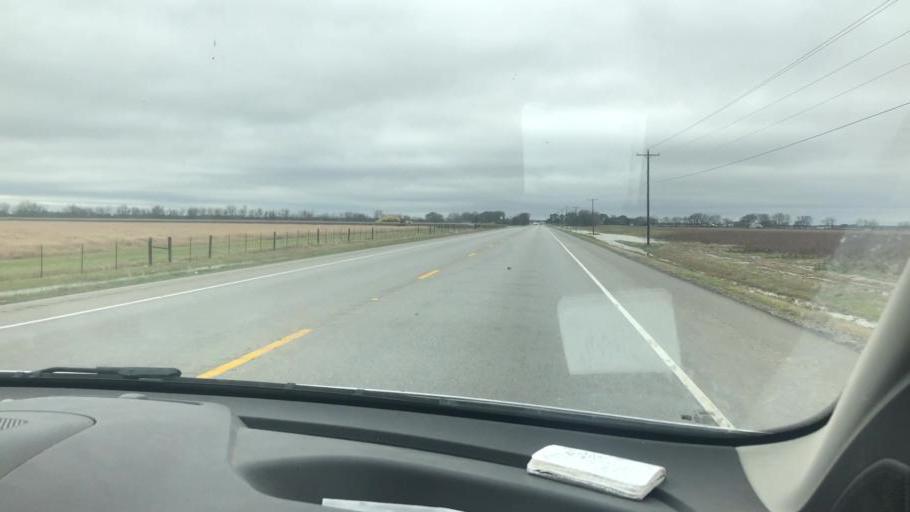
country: US
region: Texas
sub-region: Matagorda County
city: Bay City
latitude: 29.0515
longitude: -95.9710
